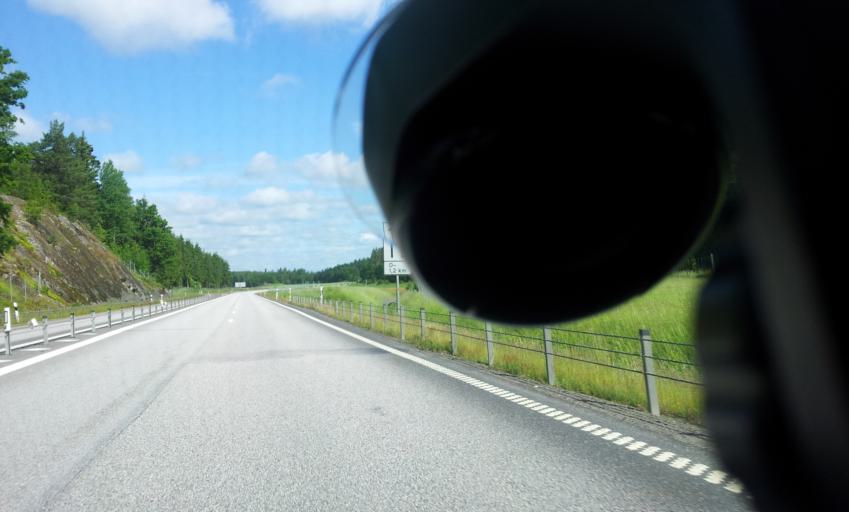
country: SE
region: OEstergoetland
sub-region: Soderkopings Kommun
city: Soederkoeping
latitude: 58.3833
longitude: 16.4151
